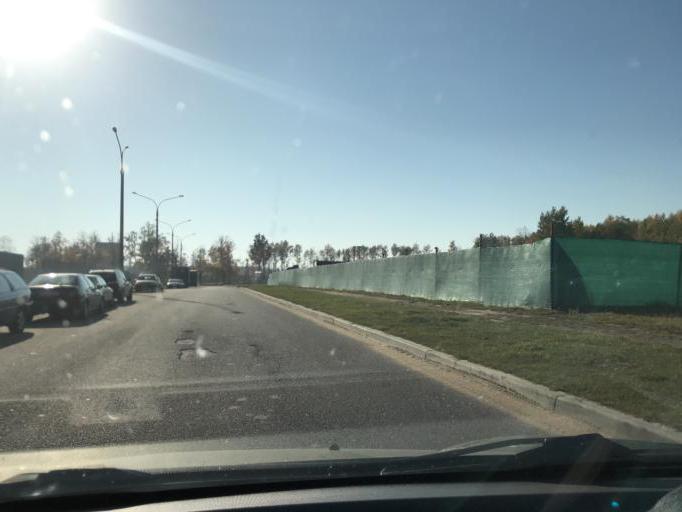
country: BY
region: Minsk
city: Pryvol'ny
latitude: 53.8126
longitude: 27.7853
